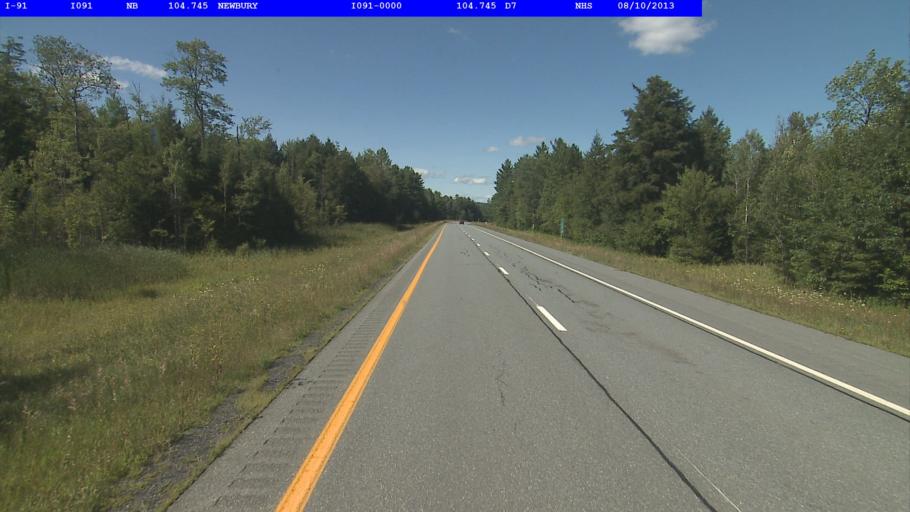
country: US
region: New Hampshire
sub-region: Grafton County
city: Haverhill
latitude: 44.0817
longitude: -72.1121
